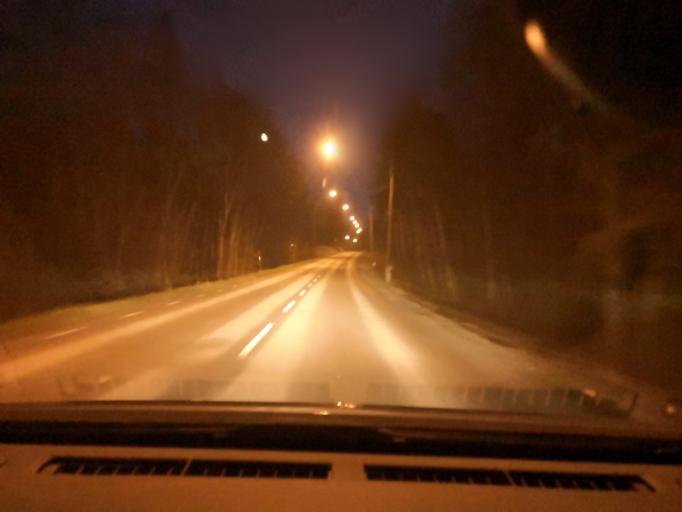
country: SE
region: OErebro
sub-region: Orebro Kommun
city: Orebro
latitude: 59.2508
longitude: 15.2789
